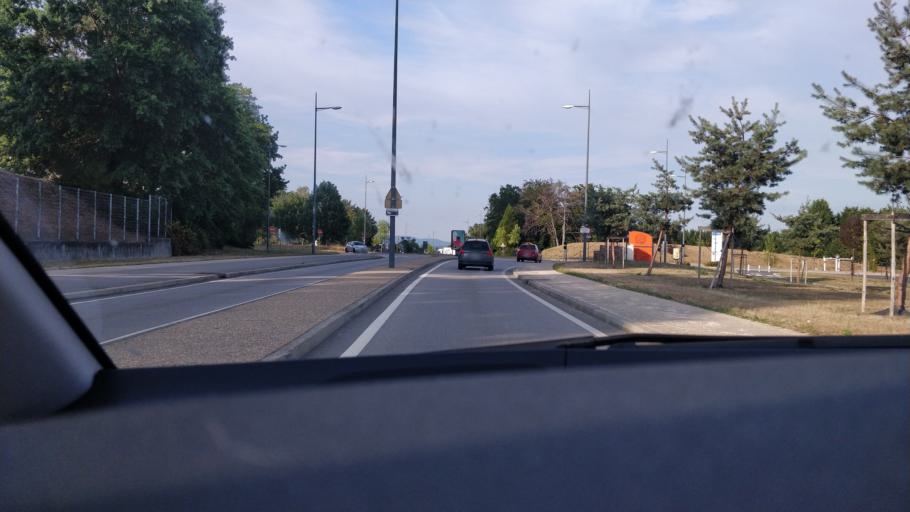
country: FR
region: Limousin
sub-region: Departement de la Haute-Vienne
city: Le Palais-sur-Vienne
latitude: 45.8709
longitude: 1.2992
